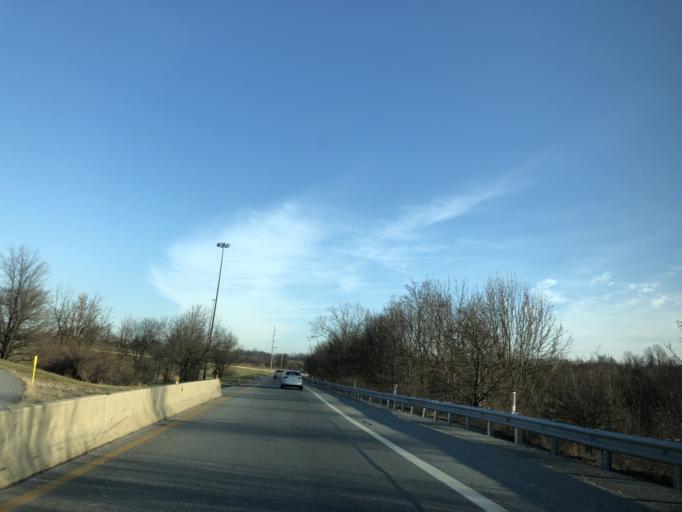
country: US
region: Pennsylvania
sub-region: Chester County
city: Exton
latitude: 40.0625
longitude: -75.6719
